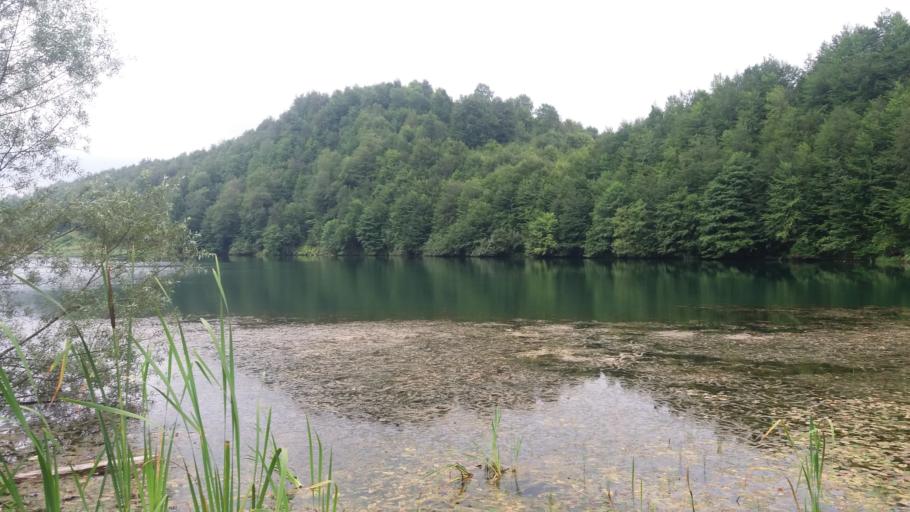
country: TR
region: Ordu
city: Golkoy
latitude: 40.6320
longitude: 37.5460
